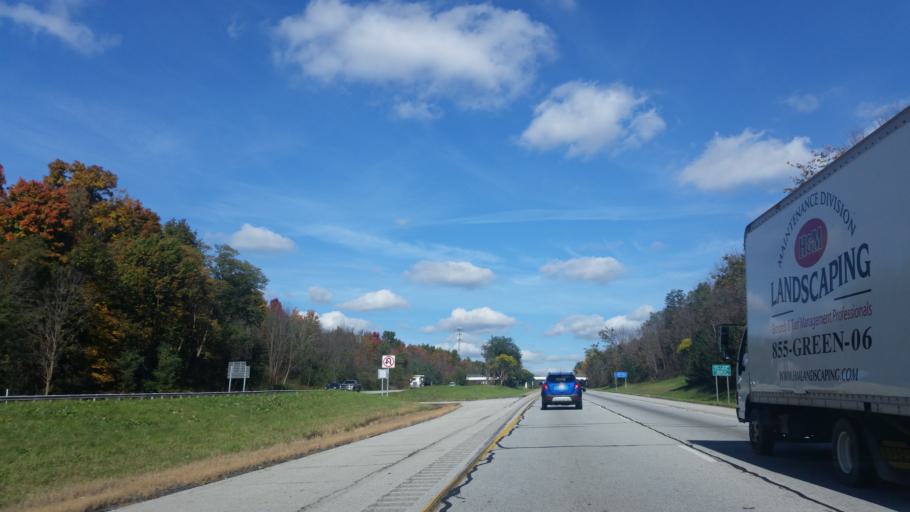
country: US
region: Ohio
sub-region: Summit County
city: Montrose-Ghent
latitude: 41.1593
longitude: -81.6261
